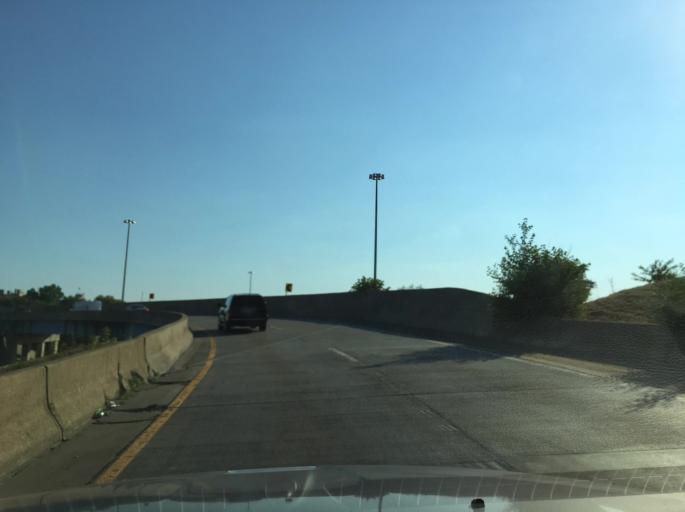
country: US
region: Michigan
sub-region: Wayne County
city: Hamtramck
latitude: 42.3681
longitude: -83.0594
